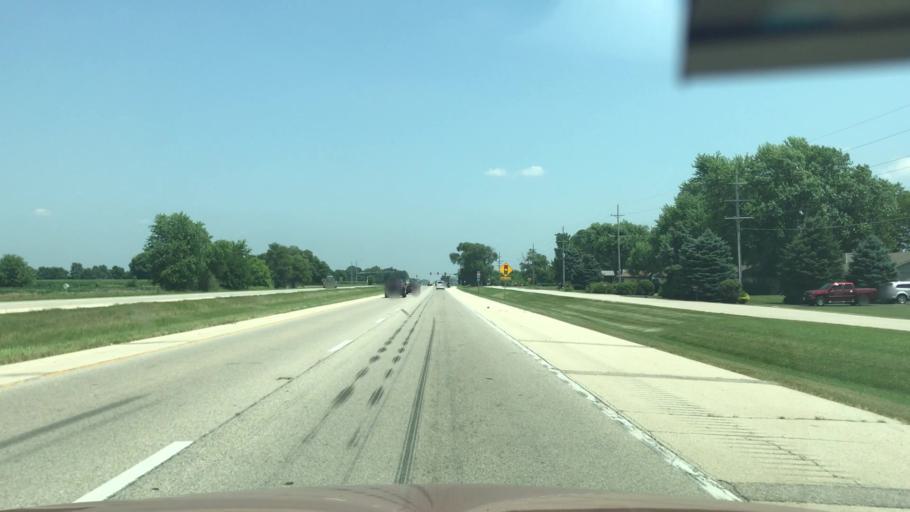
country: US
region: Illinois
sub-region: Winnebago County
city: Cherry Valley
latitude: 42.2398
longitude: -88.9057
